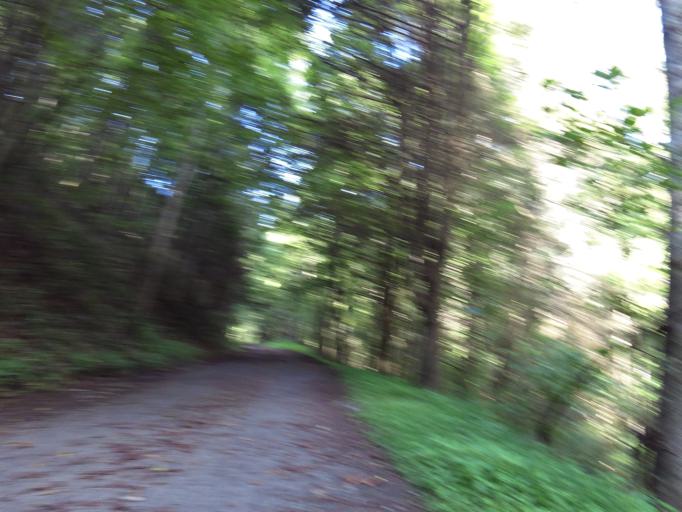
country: US
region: Virginia
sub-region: Washington County
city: Abingdon
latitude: 36.6886
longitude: -81.9394
